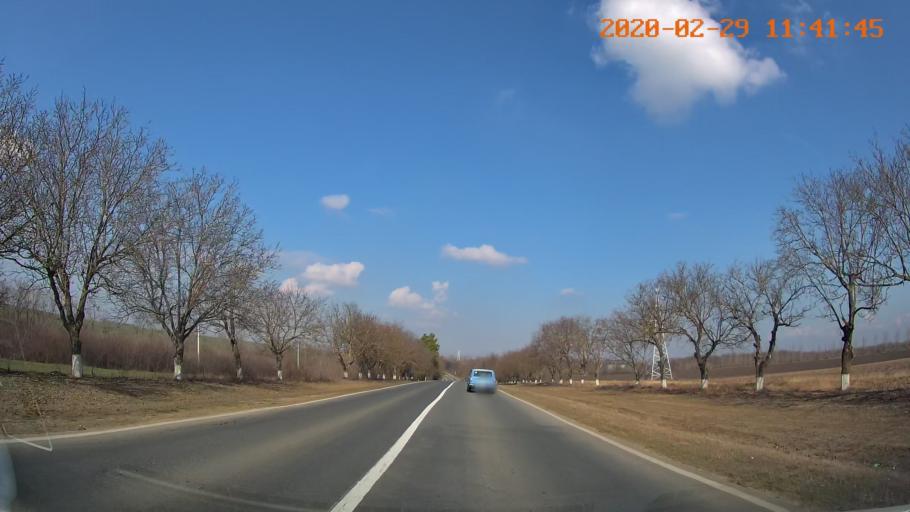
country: MD
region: Rezina
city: Saharna
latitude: 47.6760
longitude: 29.0153
